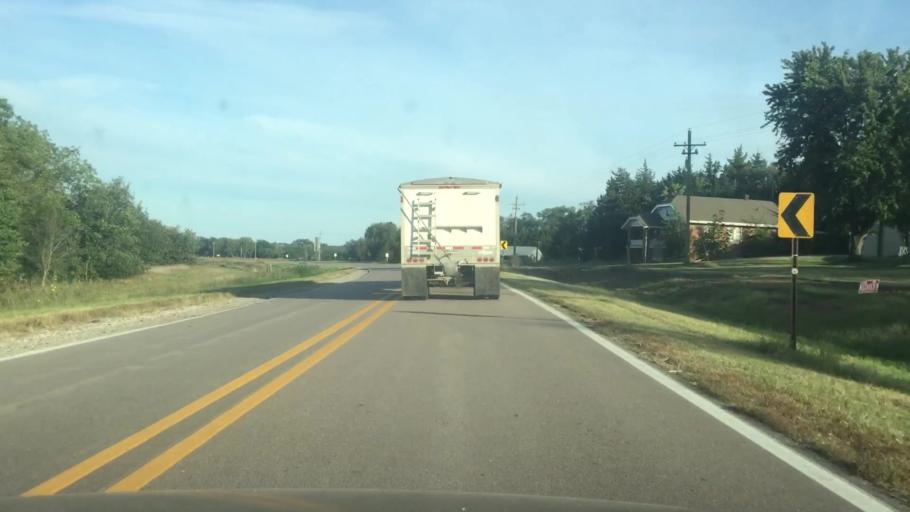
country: US
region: Nebraska
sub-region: Jefferson County
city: Fairbury
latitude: 40.0476
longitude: -97.0253
